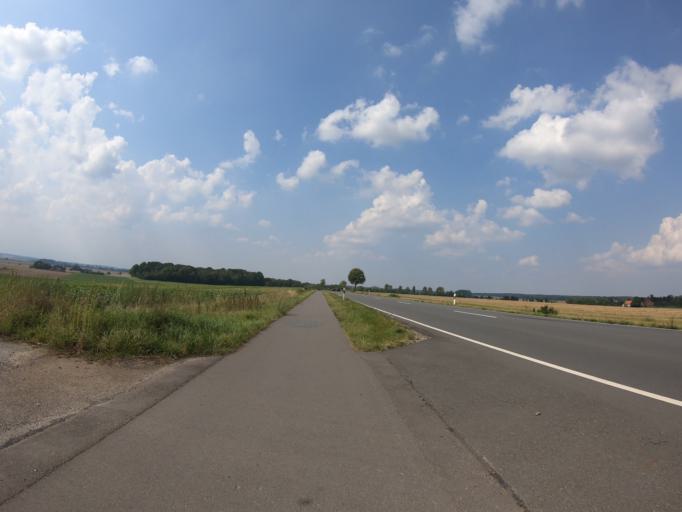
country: DE
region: Lower Saxony
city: Veltheim
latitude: 52.2073
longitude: 10.6707
